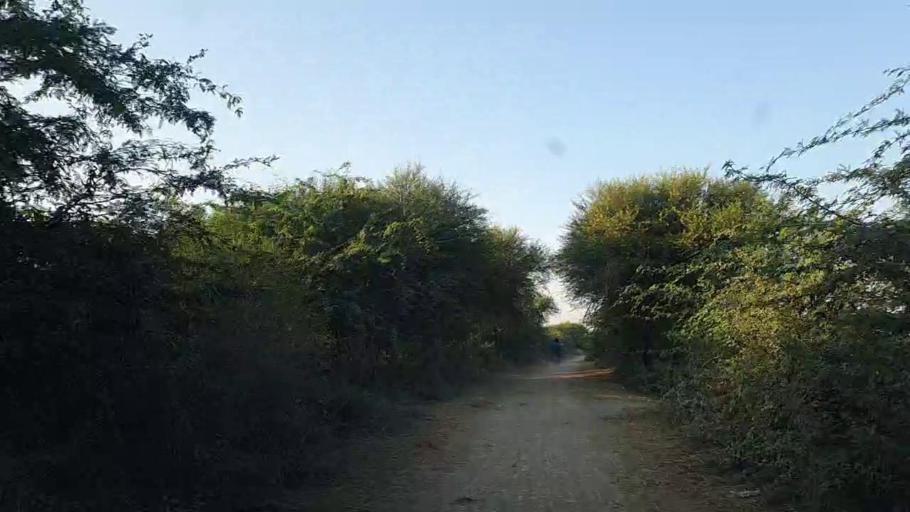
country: PK
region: Sindh
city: Mirpur Batoro
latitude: 24.7176
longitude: 68.2144
